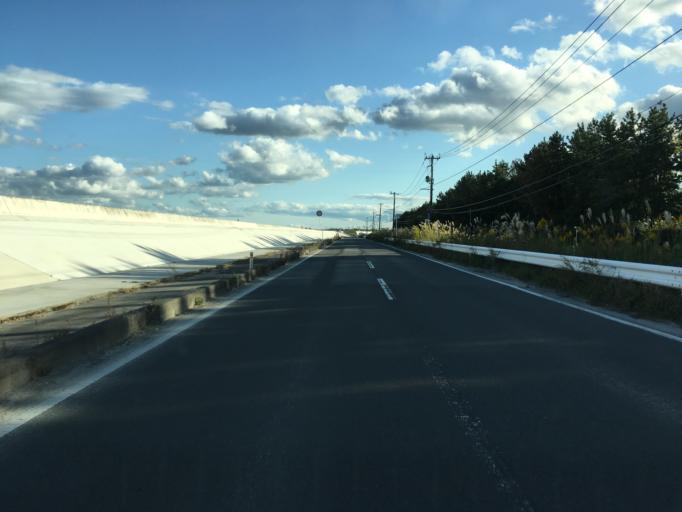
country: JP
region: Miyagi
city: Marumori
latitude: 37.8465
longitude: 140.9484
